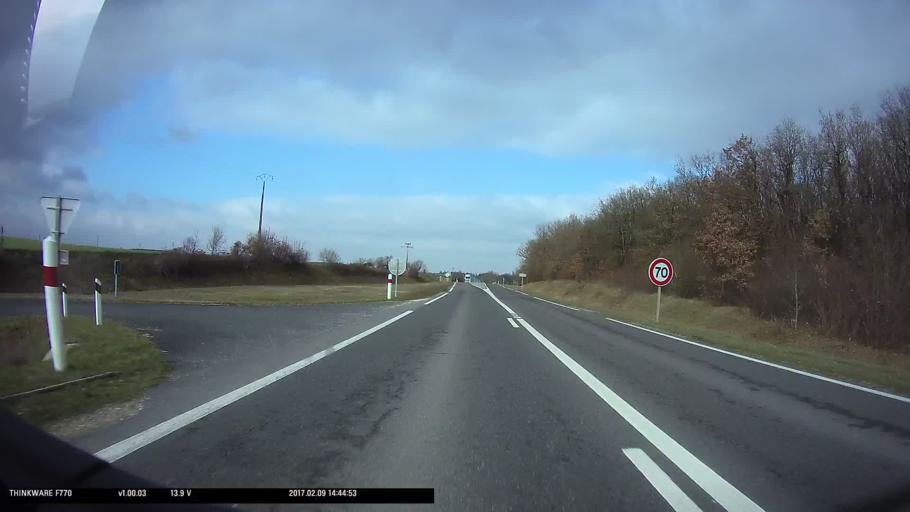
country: FR
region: Centre
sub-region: Departement du Cher
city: Trouy
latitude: 47.0082
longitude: 2.3927
